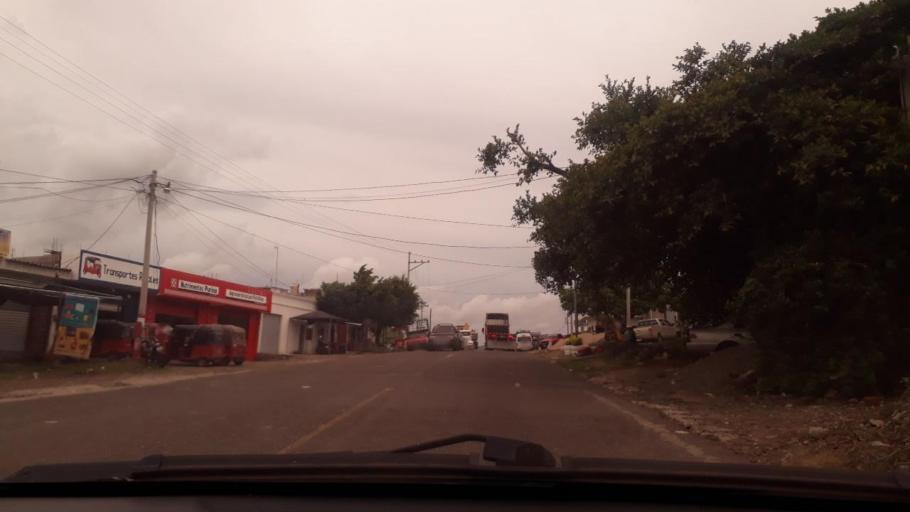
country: GT
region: Chiquimula
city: Ipala
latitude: 14.6229
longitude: -89.6285
